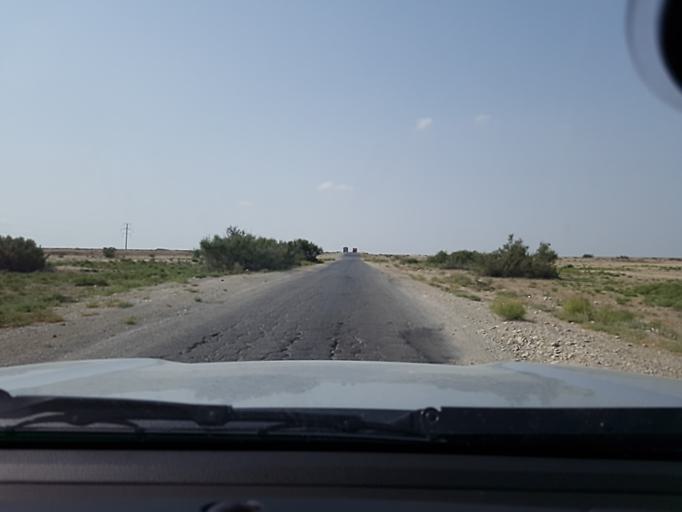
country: TM
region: Balkan
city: Gumdag
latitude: 38.9353
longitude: 54.5903
